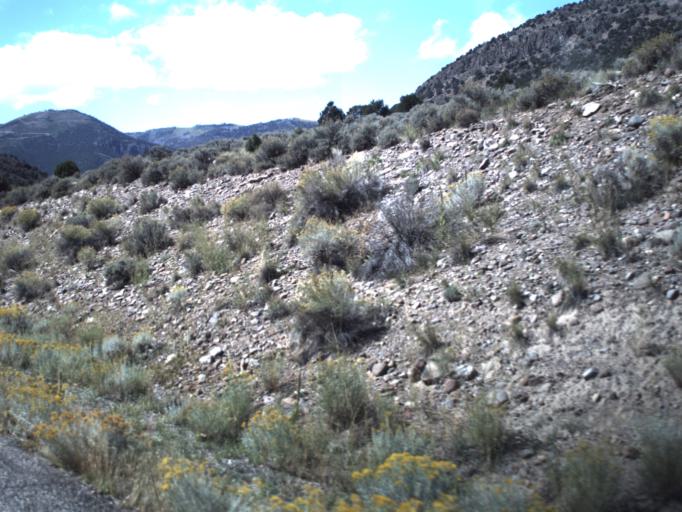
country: US
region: Utah
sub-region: Piute County
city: Junction
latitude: 38.2582
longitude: -112.2664
